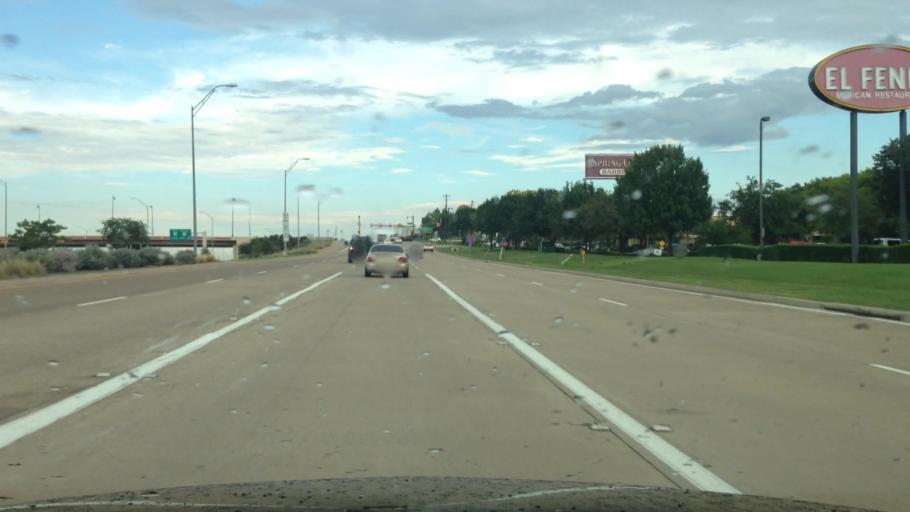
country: US
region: Texas
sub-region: Tarrant County
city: Grapevine
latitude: 32.9220
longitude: -97.0820
